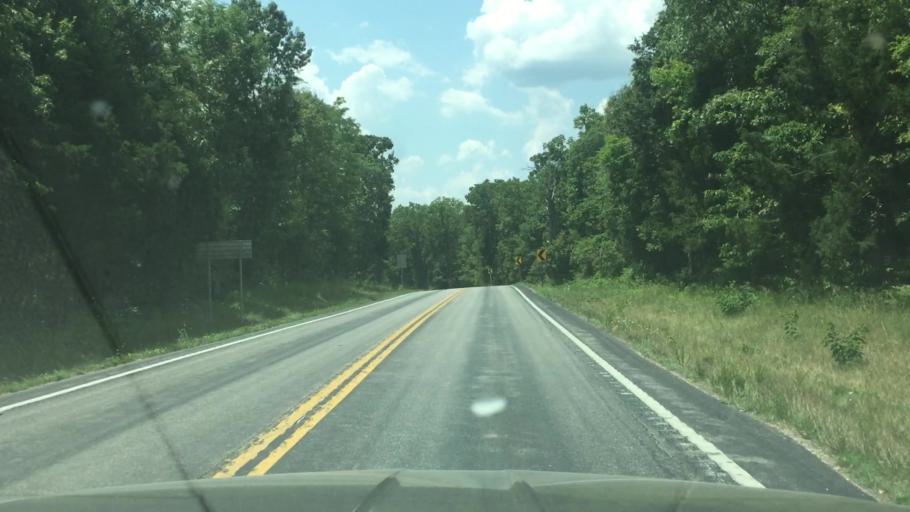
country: US
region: Missouri
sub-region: Camden County
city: Osage Beach
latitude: 38.1285
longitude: -92.5573
